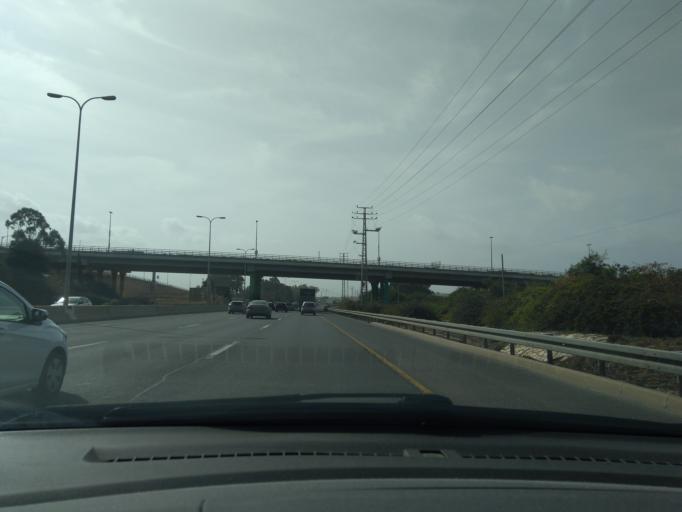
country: IL
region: Central District
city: Netanya
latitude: 32.3132
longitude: 34.8656
